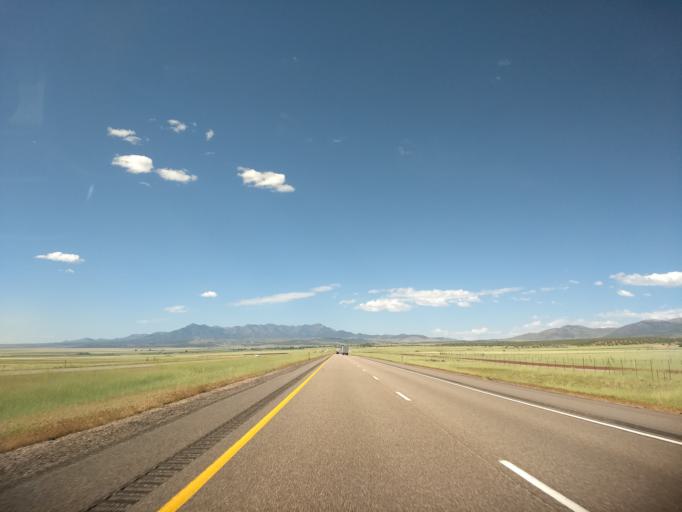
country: US
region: Utah
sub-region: Millard County
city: Fillmore
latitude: 39.0569
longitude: -112.2879
